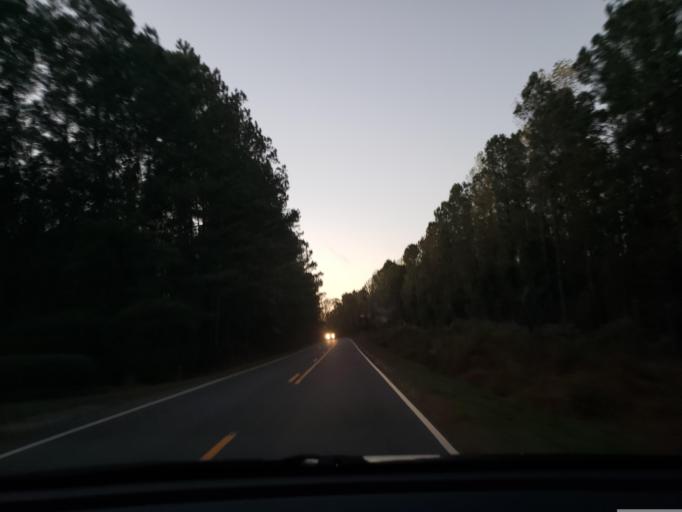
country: US
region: North Carolina
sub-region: Duplin County
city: Beulaville
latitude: 34.7858
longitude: -77.7567
